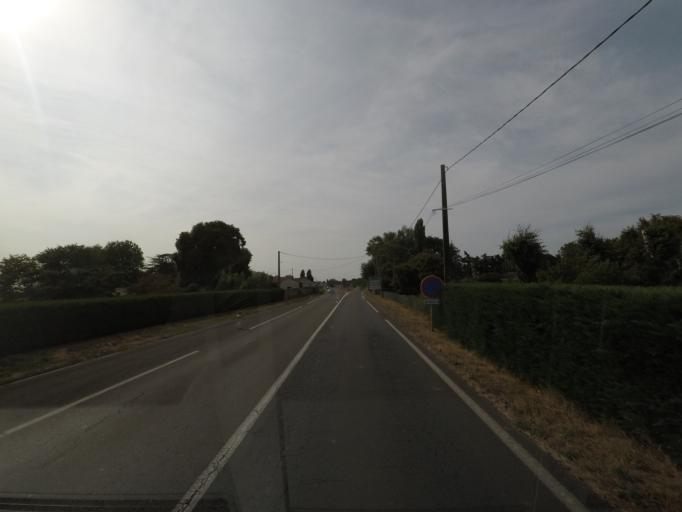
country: FR
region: Poitou-Charentes
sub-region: Departement des Deux-Sevres
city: Melle
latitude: 46.2033
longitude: -0.0917
